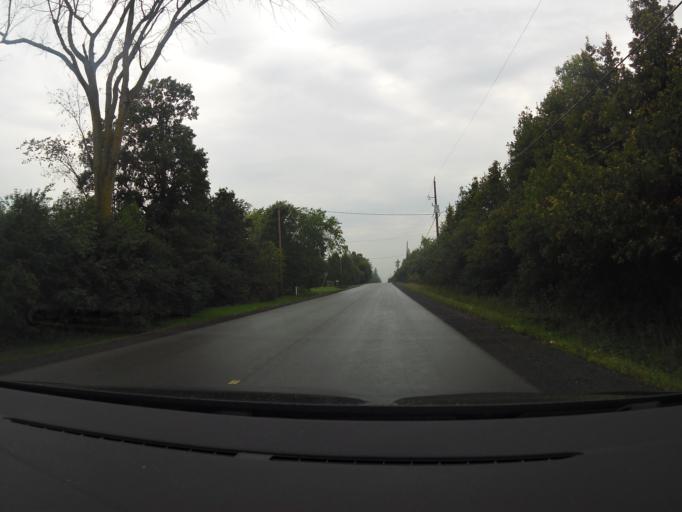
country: CA
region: Ontario
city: Carleton Place
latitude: 45.1763
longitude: -76.0563
